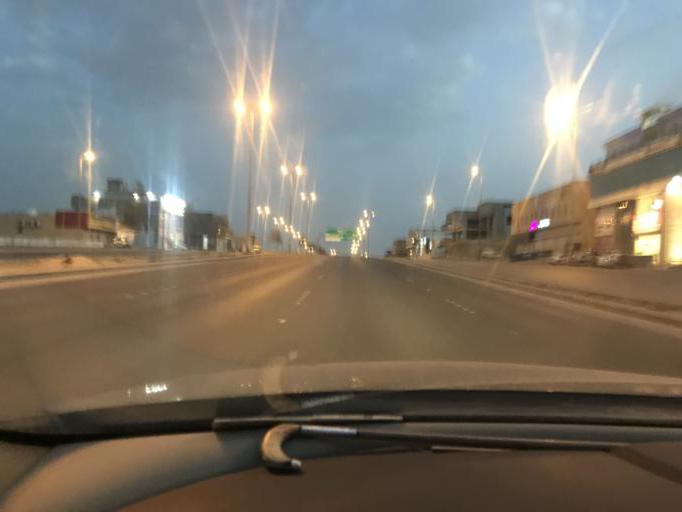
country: SA
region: Ar Riyad
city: Riyadh
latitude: 24.8409
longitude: 46.6760
